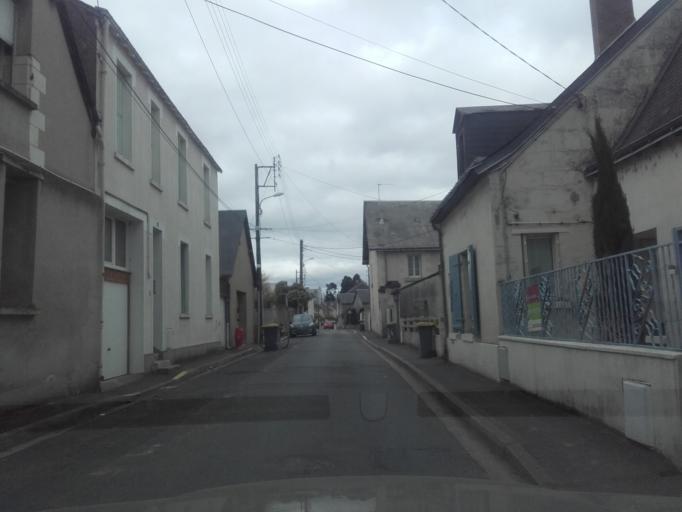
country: FR
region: Centre
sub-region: Departement d'Indre-et-Loire
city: Tours
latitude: 47.4076
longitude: 0.6945
